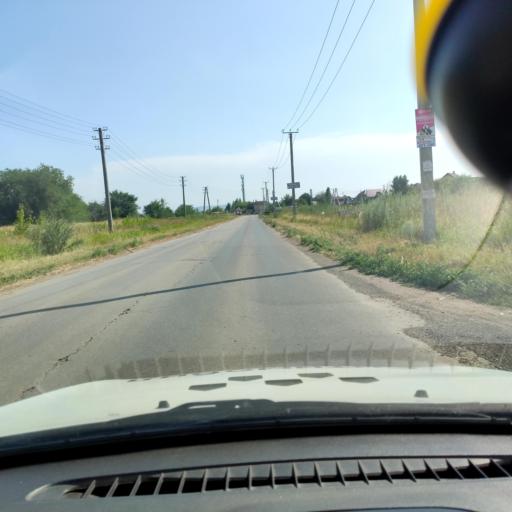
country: RU
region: Samara
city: Podstepki
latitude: 53.5140
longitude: 49.1935
